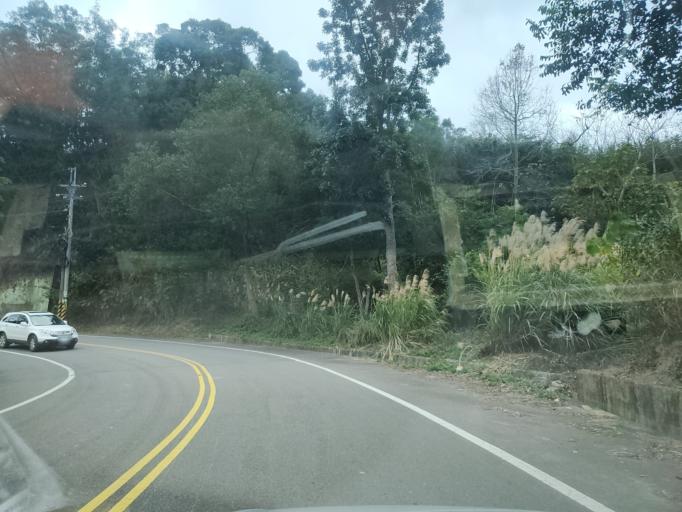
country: TW
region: Taiwan
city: Fengyuan
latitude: 24.3659
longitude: 120.7758
